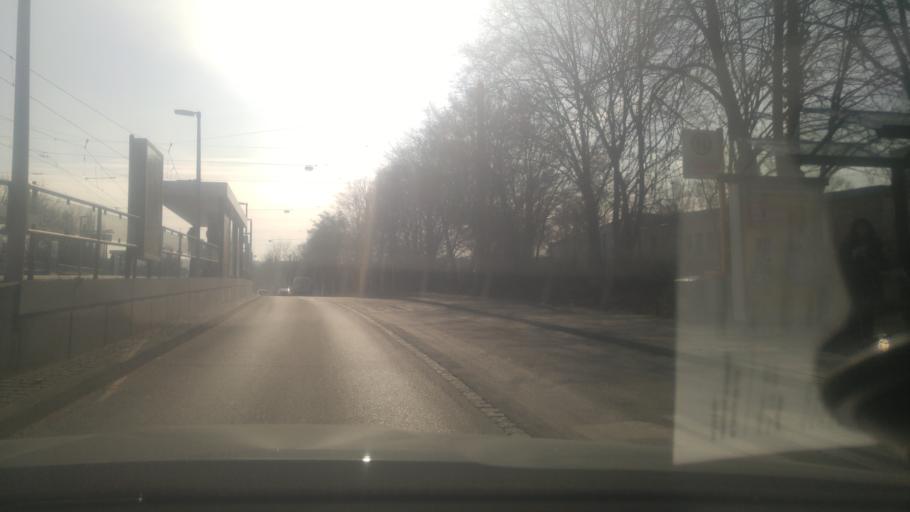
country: DE
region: Baden-Wuerttemberg
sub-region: Regierungsbezirk Stuttgart
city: Stuttgart Feuerbach
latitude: 48.8273
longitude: 9.1737
